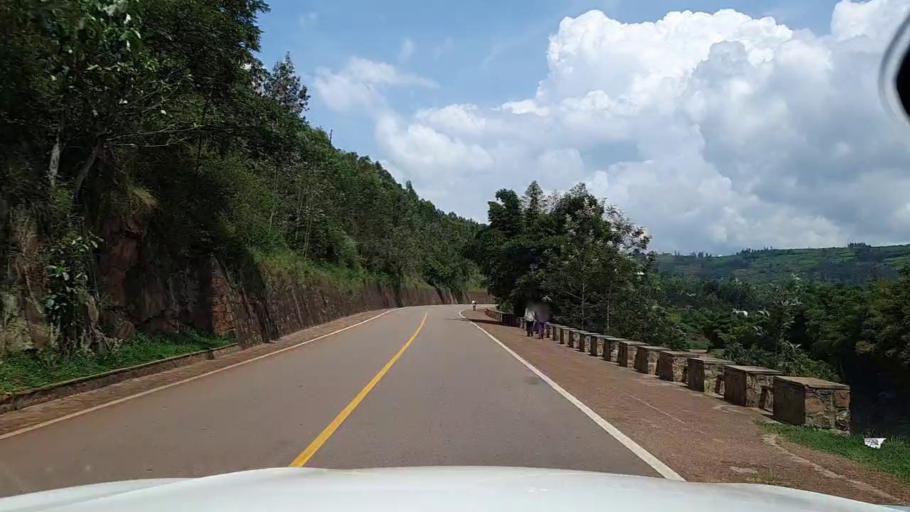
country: RW
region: Kigali
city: Kigali
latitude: -1.8297
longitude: 30.0789
